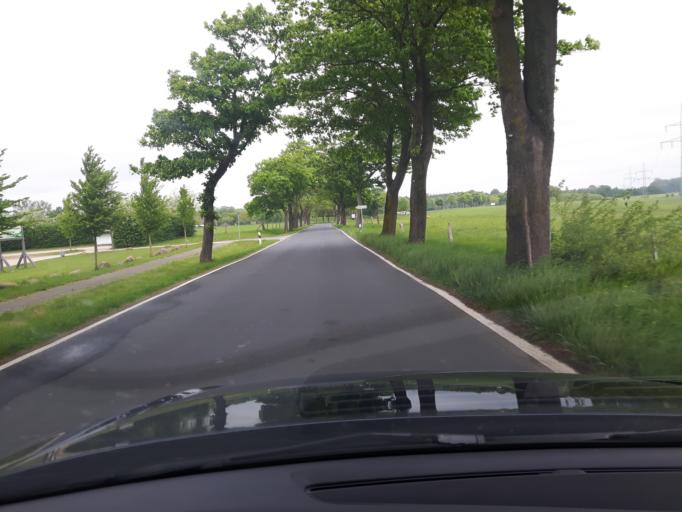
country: DE
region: Mecklenburg-Vorpommern
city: Tribsees
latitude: 54.1690
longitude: 12.7299
